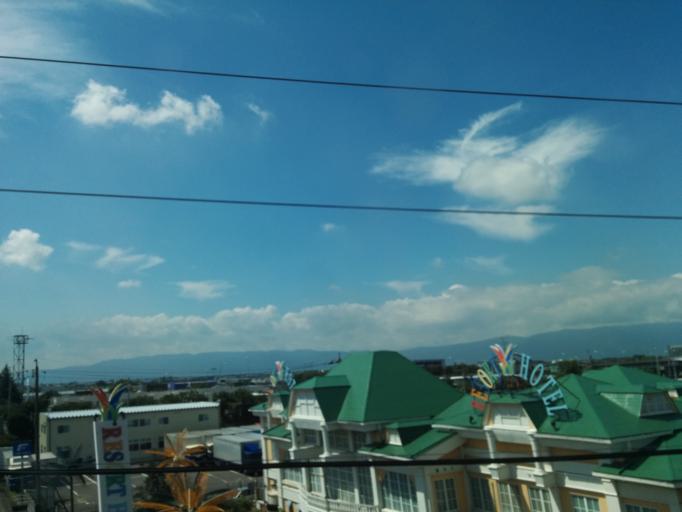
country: JP
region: Aichi
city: Sobue
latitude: 35.3083
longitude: 136.6947
